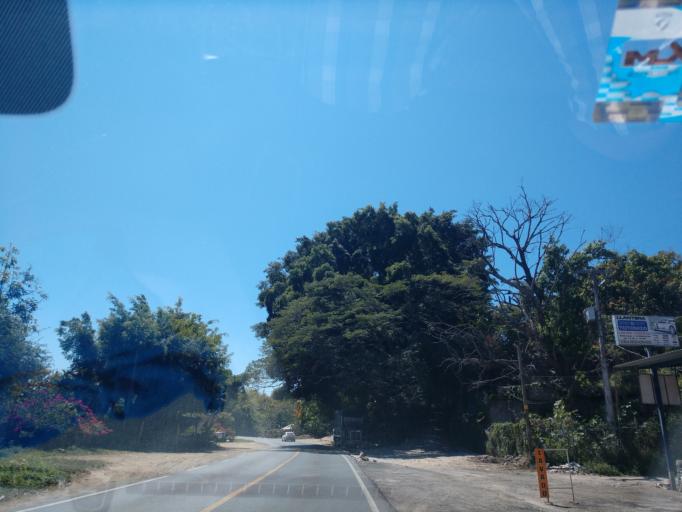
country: MX
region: Nayarit
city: Xalisco
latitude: 21.4050
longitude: -104.8963
